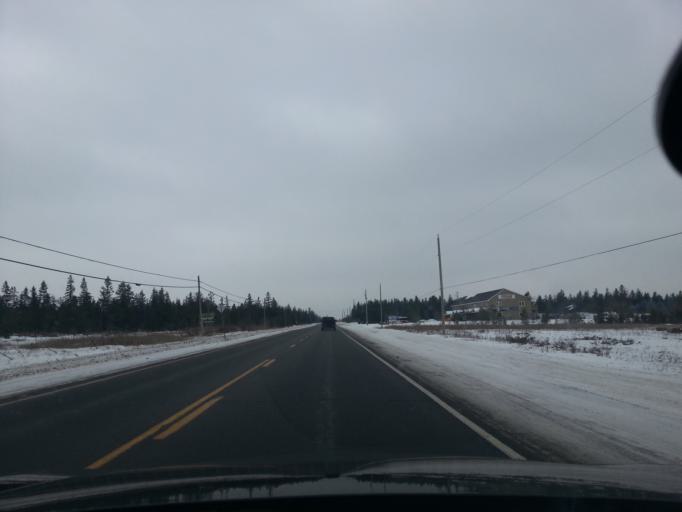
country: CA
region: Ontario
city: Carleton Place
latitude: 45.2503
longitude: -76.1595
